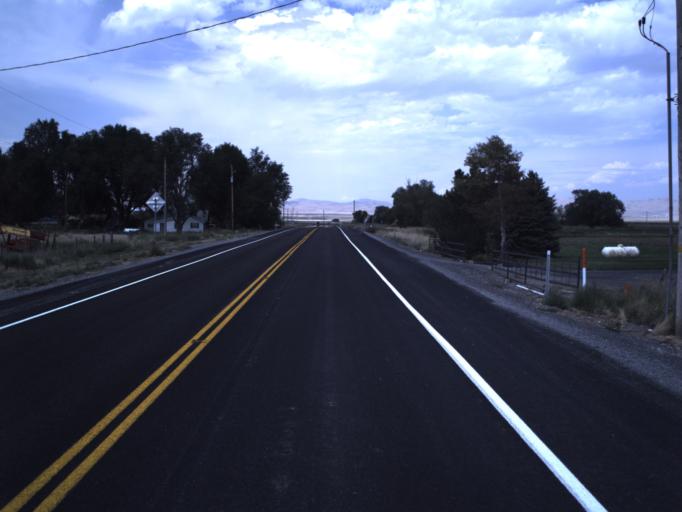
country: US
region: Utah
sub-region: Utah County
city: Eagle Mountain
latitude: 40.2642
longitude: -112.0941
